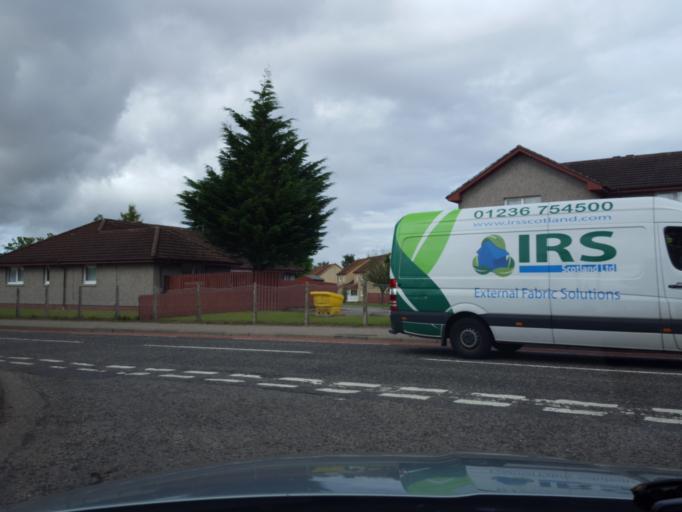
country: GB
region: Scotland
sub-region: Moray
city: Kinloss
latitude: 57.6356
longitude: -3.5652
